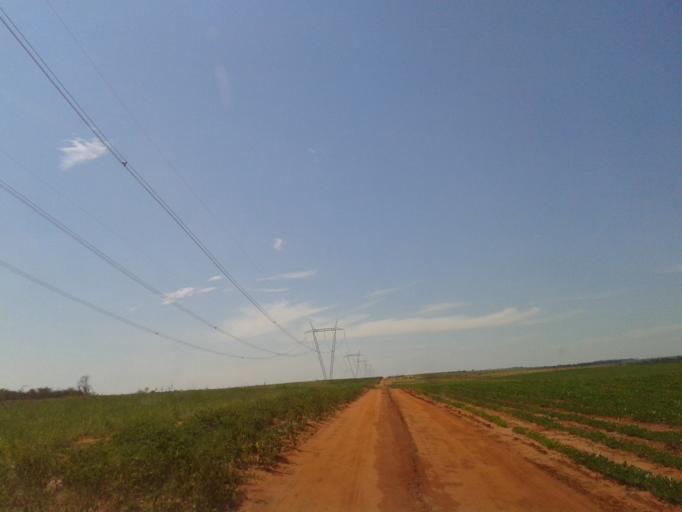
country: BR
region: Minas Gerais
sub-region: Santa Vitoria
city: Santa Vitoria
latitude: -19.0708
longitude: -50.4628
